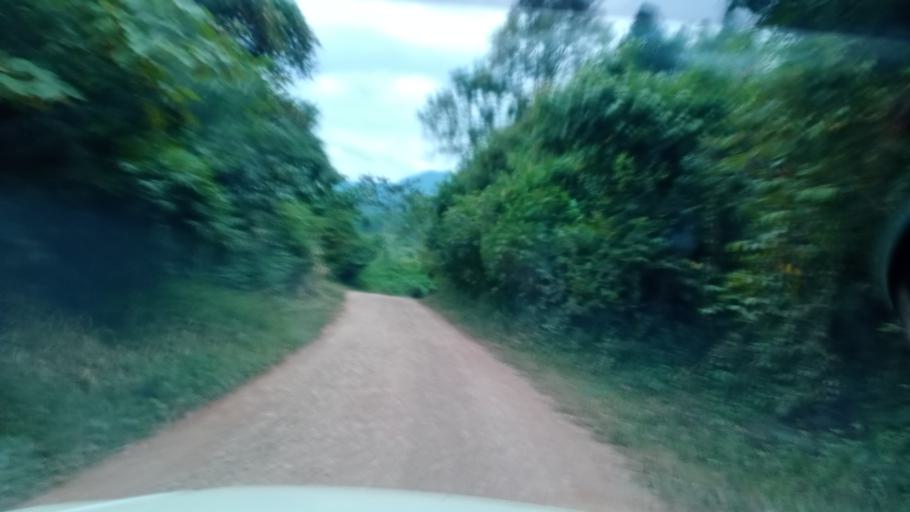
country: TH
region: Changwat Bueng Kan
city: Pak Khat
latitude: 18.7159
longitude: 103.2222
